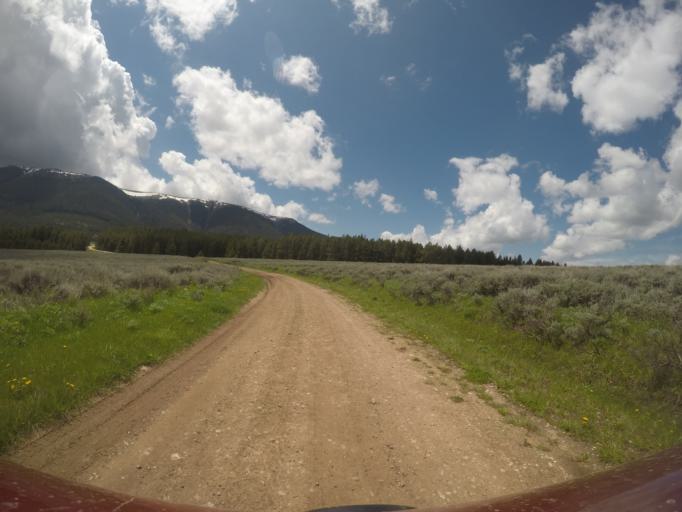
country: US
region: Wyoming
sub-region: Big Horn County
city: Lovell
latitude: 45.1793
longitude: -108.4464
